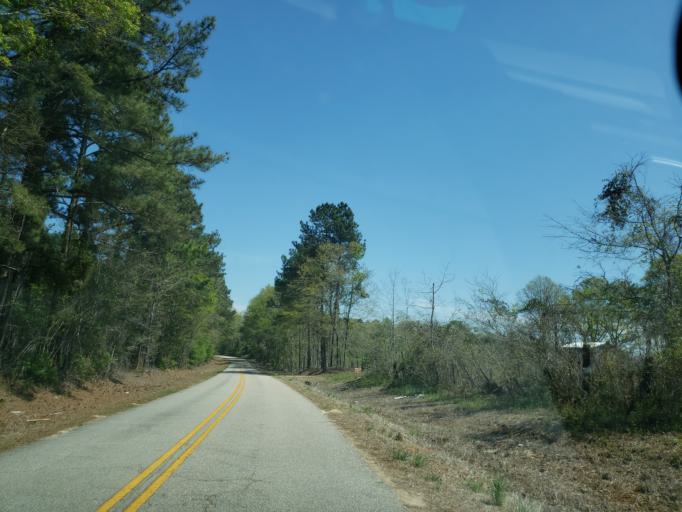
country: US
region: Alabama
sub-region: Tallapoosa County
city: Camp Hill
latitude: 32.6798
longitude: -85.6902
